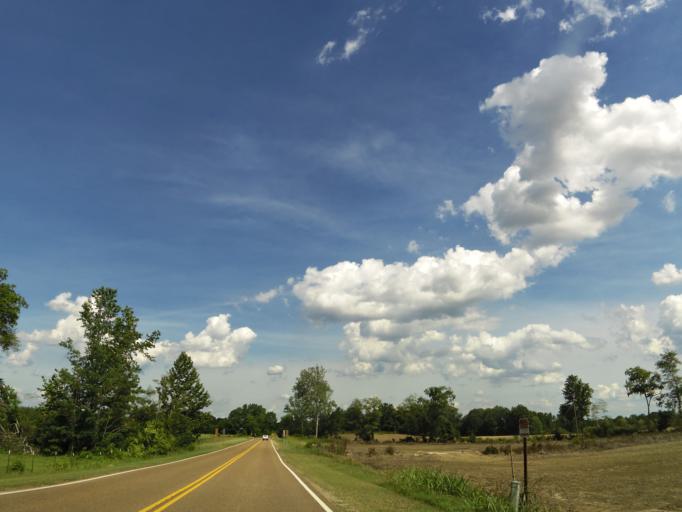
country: US
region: Tennessee
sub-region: Gibson County
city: Milan
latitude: 35.9783
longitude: -88.7583
